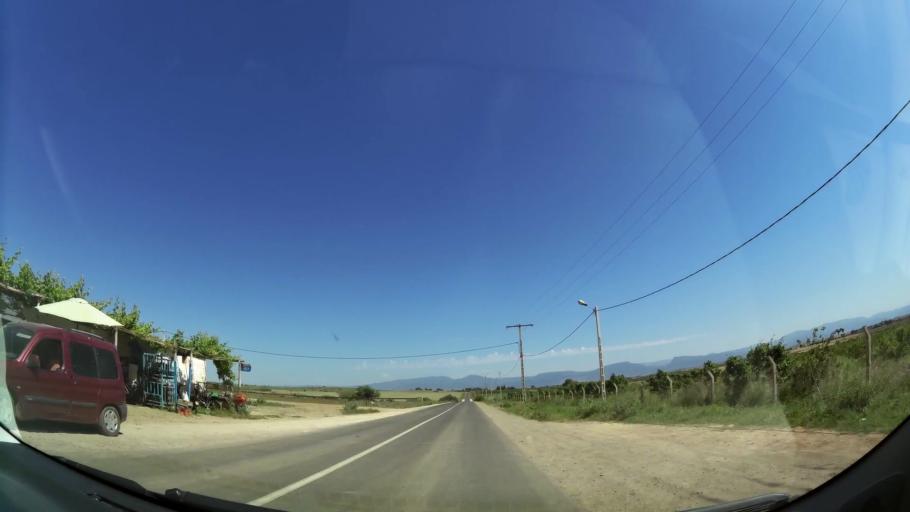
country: MA
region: Oriental
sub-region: Berkane-Taourirt
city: Madagh
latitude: 35.0358
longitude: -2.4194
